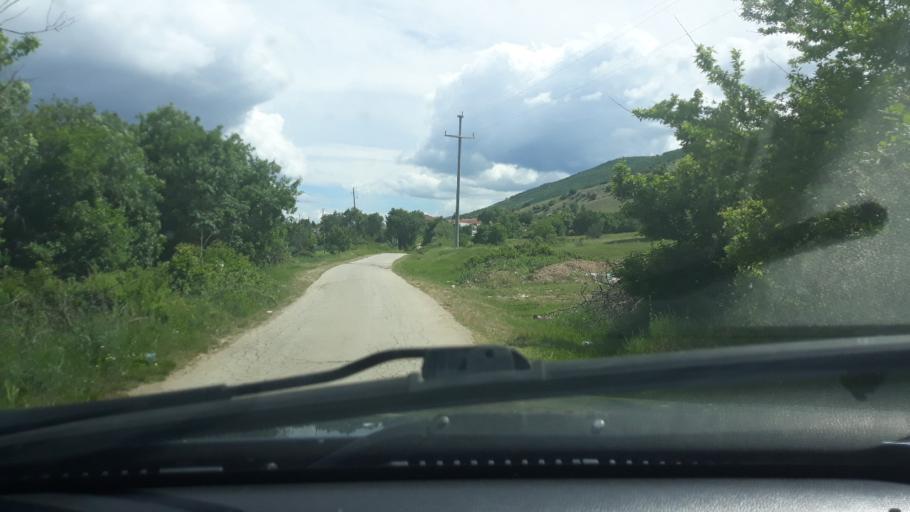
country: MK
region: Krivogastani
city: Krivogashtani
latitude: 41.3268
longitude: 21.3034
